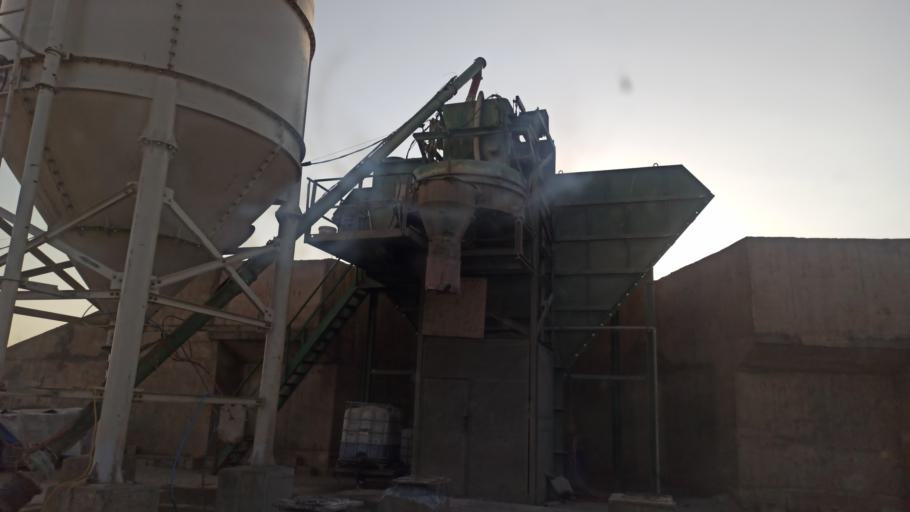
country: ET
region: Oromiya
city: Ziway
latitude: 7.6987
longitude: 38.6568
